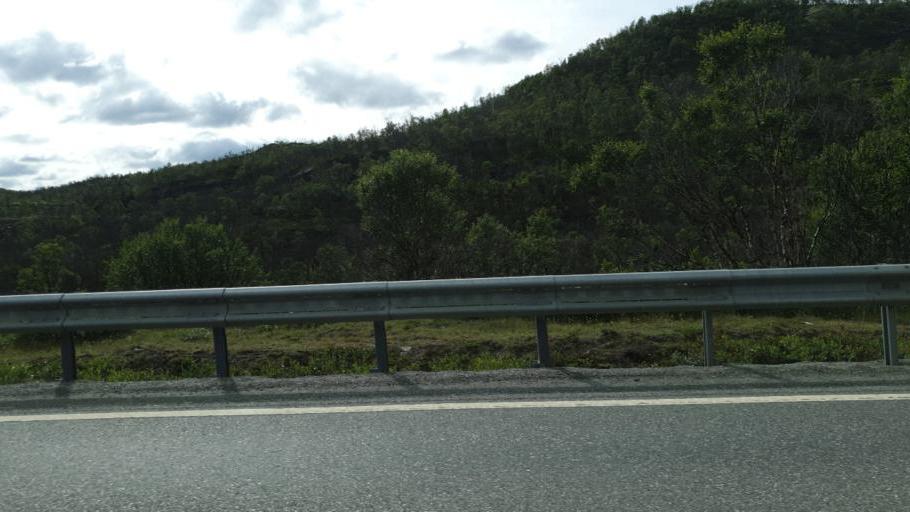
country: NO
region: Sor-Trondelag
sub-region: Oppdal
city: Oppdal
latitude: 62.2936
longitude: 9.5946
